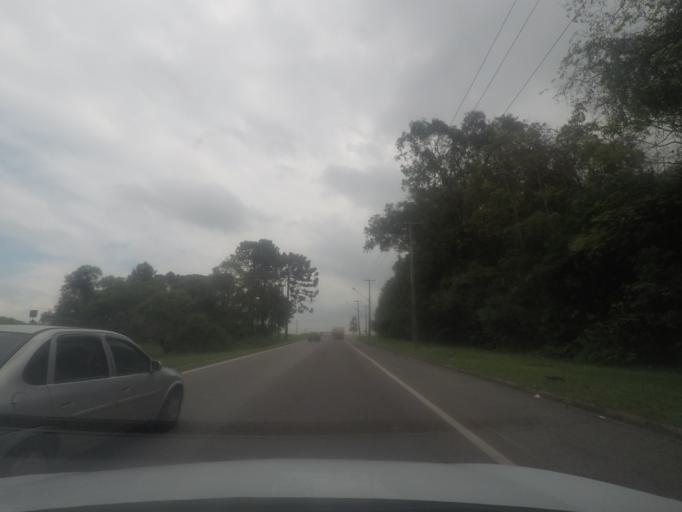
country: BR
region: Parana
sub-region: Sao Jose Dos Pinhais
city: Sao Jose dos Pinhais
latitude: -25.5424
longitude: -49.3045
